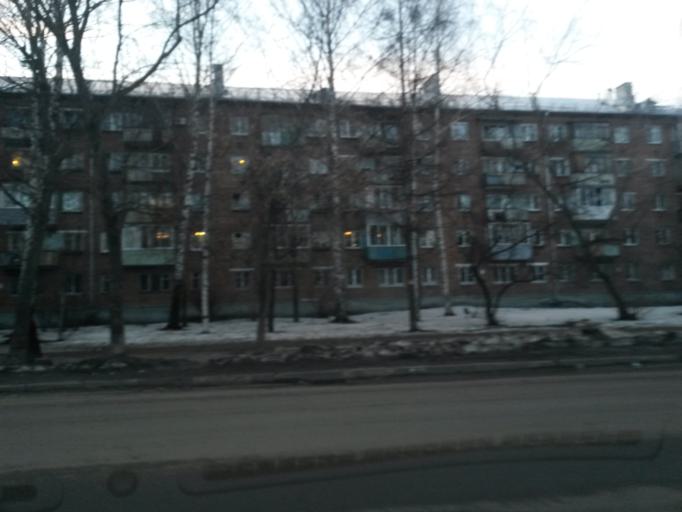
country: RU
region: Jaroslavl
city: Yaroslavl
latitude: 57.6342
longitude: 39.8362
